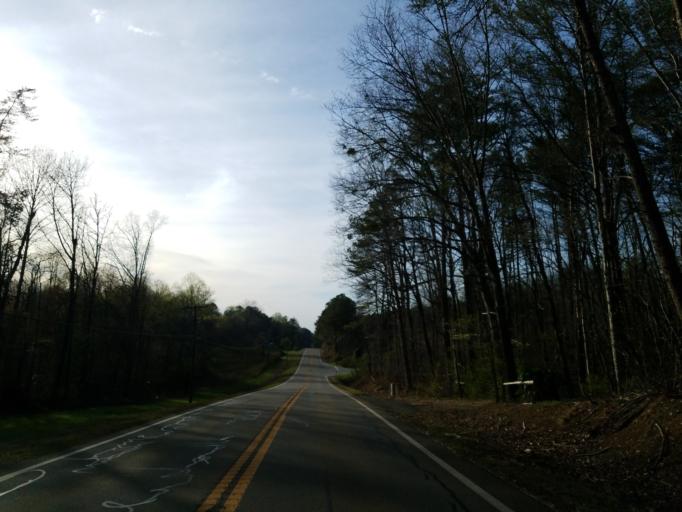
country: US
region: Georgia
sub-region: Pickens County
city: Jasper
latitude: 34.5137
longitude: -84.4553
